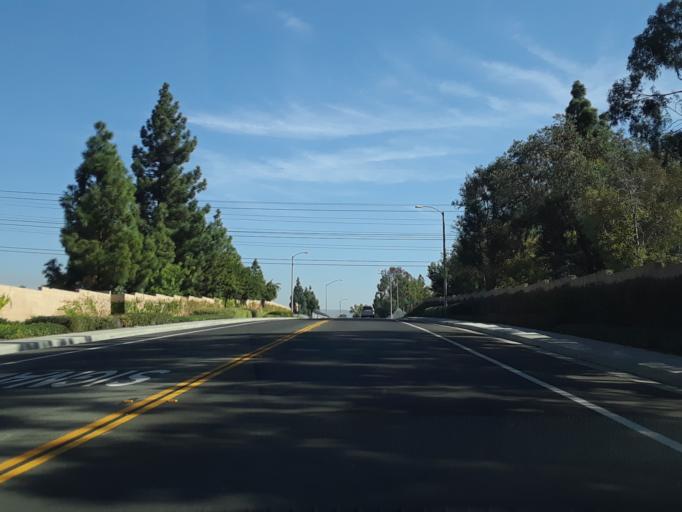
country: US
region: California
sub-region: Orange County
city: Irvine
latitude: 33.6904
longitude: -117.7841
